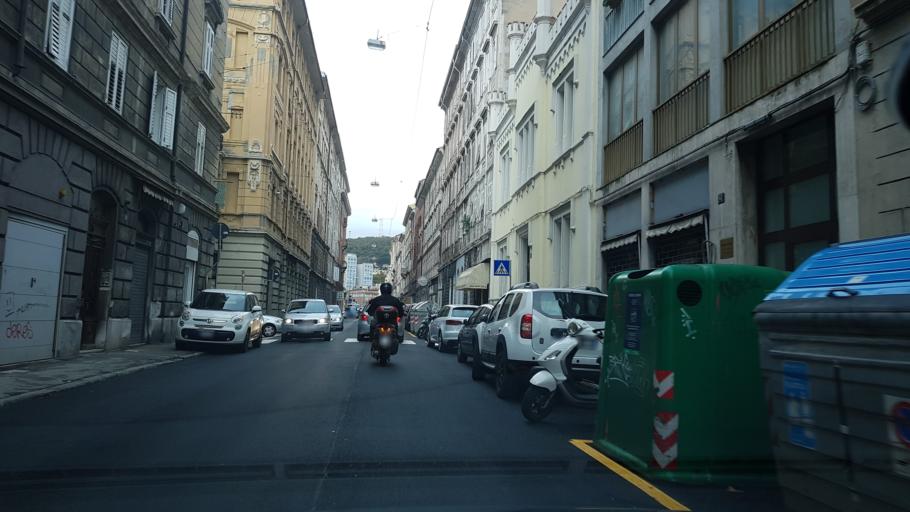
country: IT
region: Friuli Venezia Giulia
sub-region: Provincia di Trieste
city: Trieste
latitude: 45.6604
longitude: 13.7725
